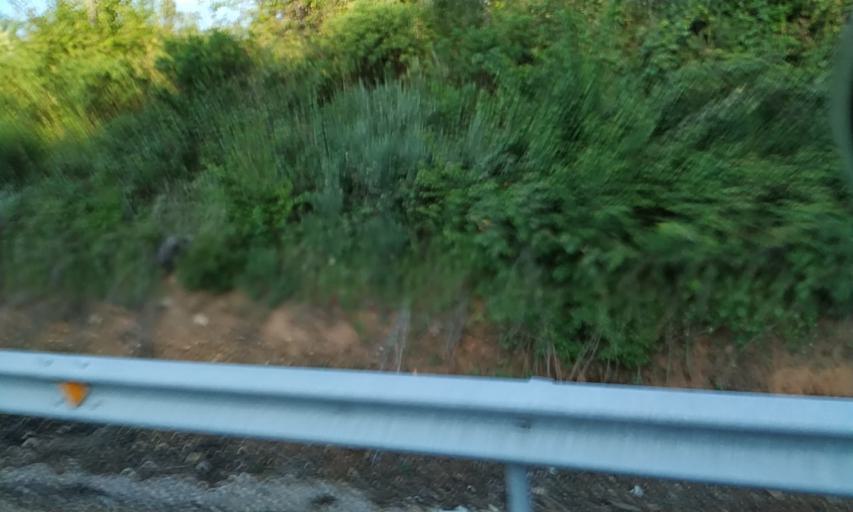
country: PT
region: Portalegre
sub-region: Portalegre
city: Sao Juliao
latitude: 39.3470
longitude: -7.2756
